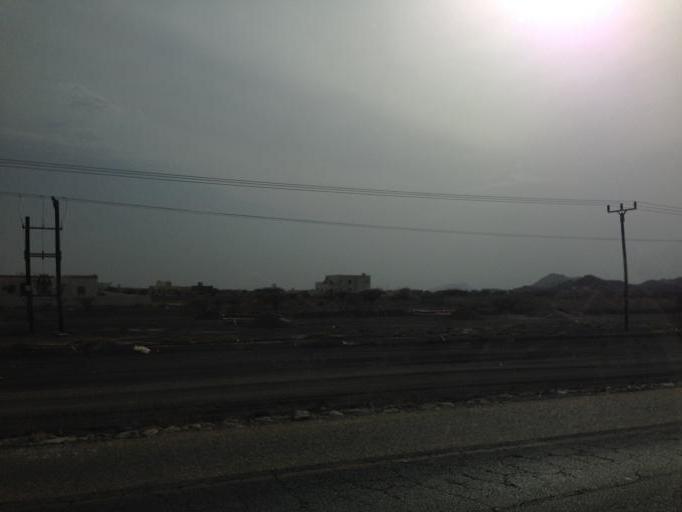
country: OM
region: Ash Sharqiyah
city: Al Qabil
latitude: 22.6311
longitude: 58.6478
